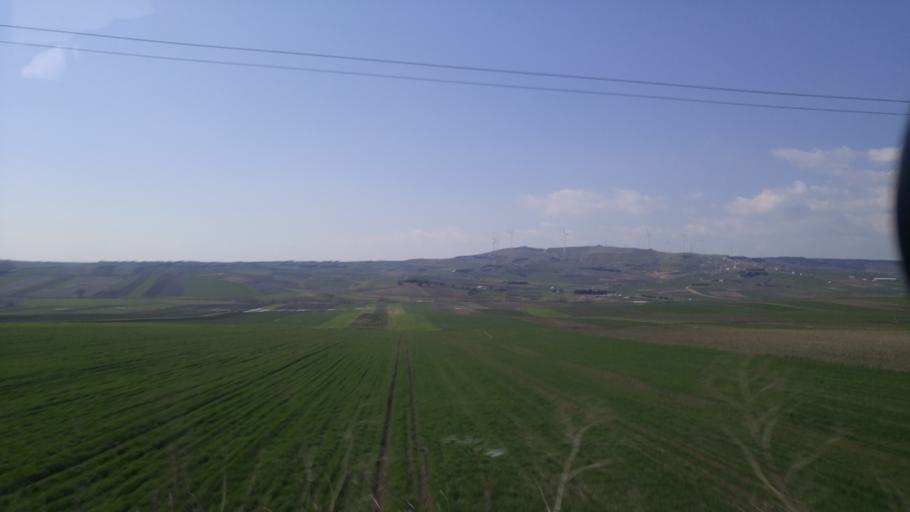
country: TR
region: Istanbul
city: Canta
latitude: 41.1018
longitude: 28.1109
